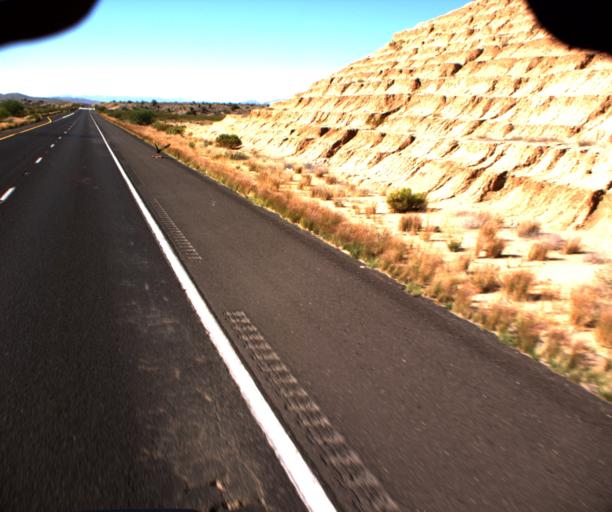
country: US
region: Arizona
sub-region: Mohave County
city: Kingman
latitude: 35.0829
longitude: -113.6661
